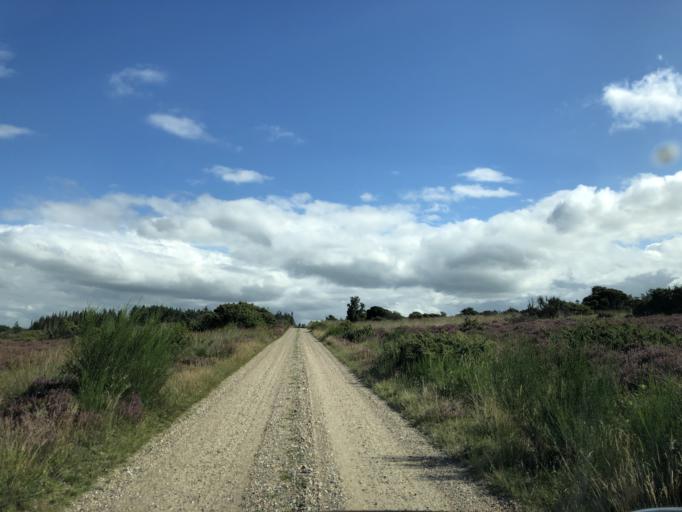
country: DK
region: Central Jutland
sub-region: Holstebro Kommune
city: Ulfborg
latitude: 56.2496
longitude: 8.4767
